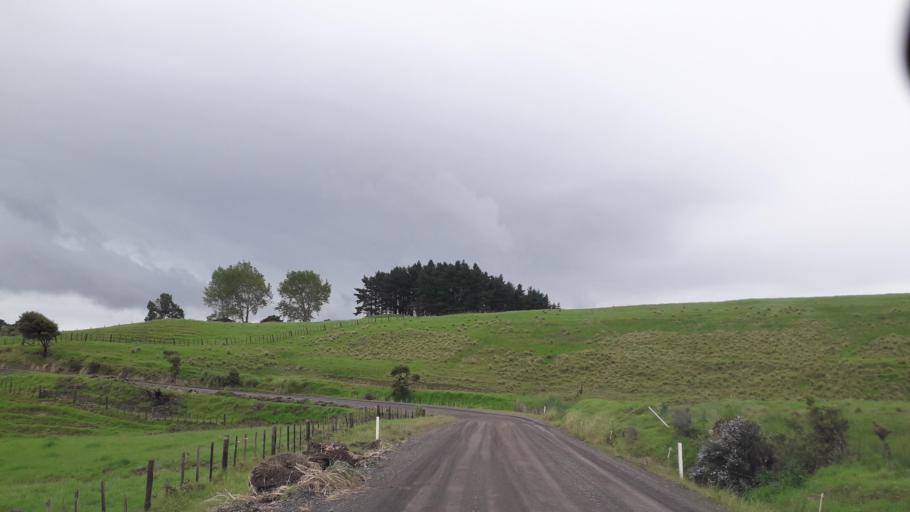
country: NZ
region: Northland
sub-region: Far North District
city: Kaitaia
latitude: -35.4086
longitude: 173.3639
